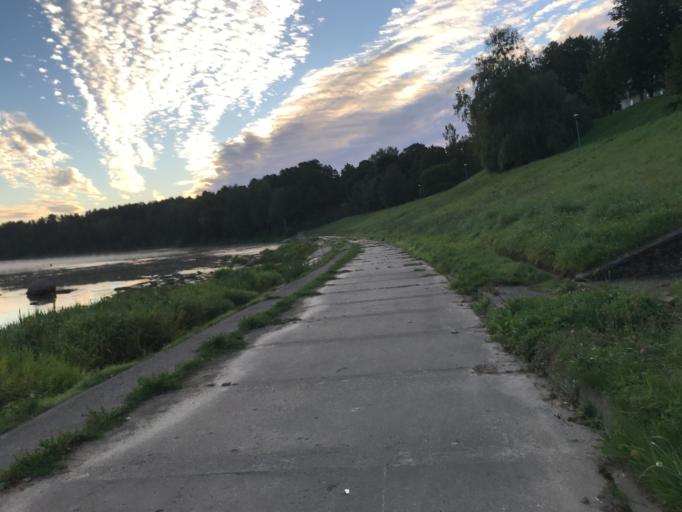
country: LT
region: Alytaus apskritis
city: Druskininkai
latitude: 54.0189
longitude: 23.9833
